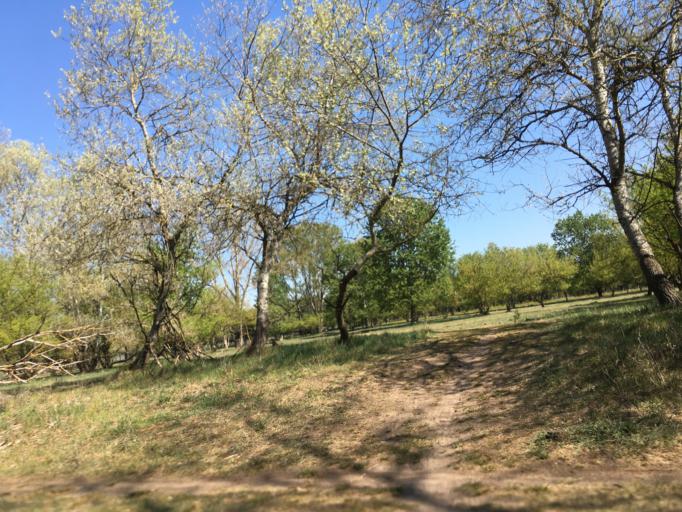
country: DE
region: Berlin
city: Blankenburg
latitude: 52.6196
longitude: 13.4548
